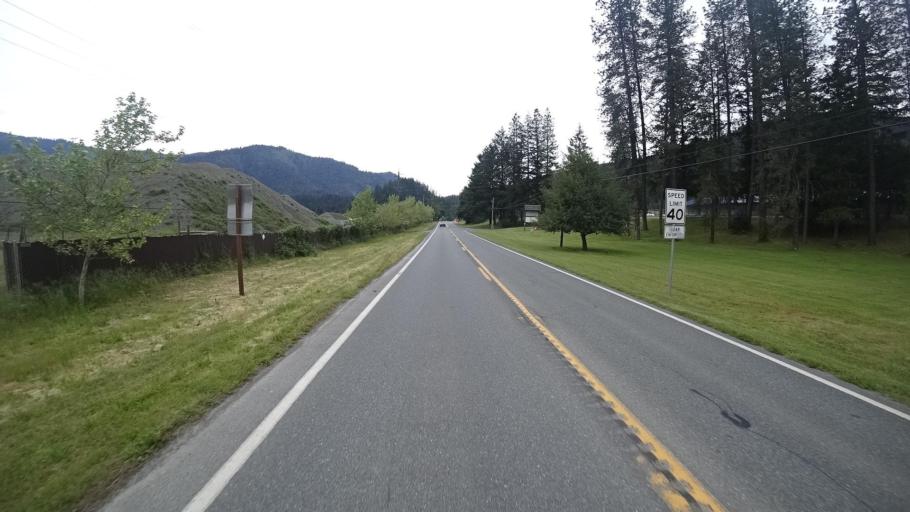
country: US
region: California
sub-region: Humboldt County
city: Willow Creek
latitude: 40.9496
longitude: -123.6382
